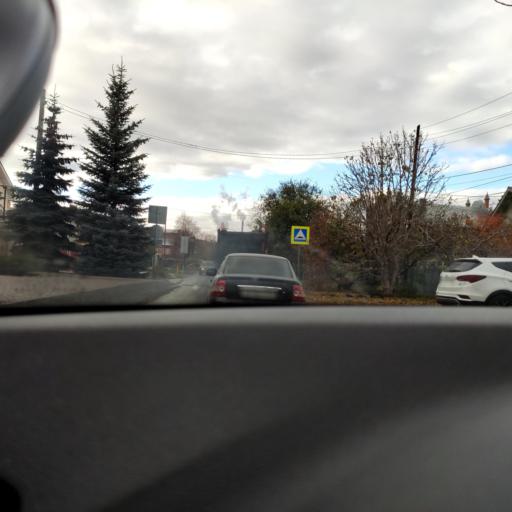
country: RU
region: Samara
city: Petra-Dubrava
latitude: 53.2488
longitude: 50.3176
